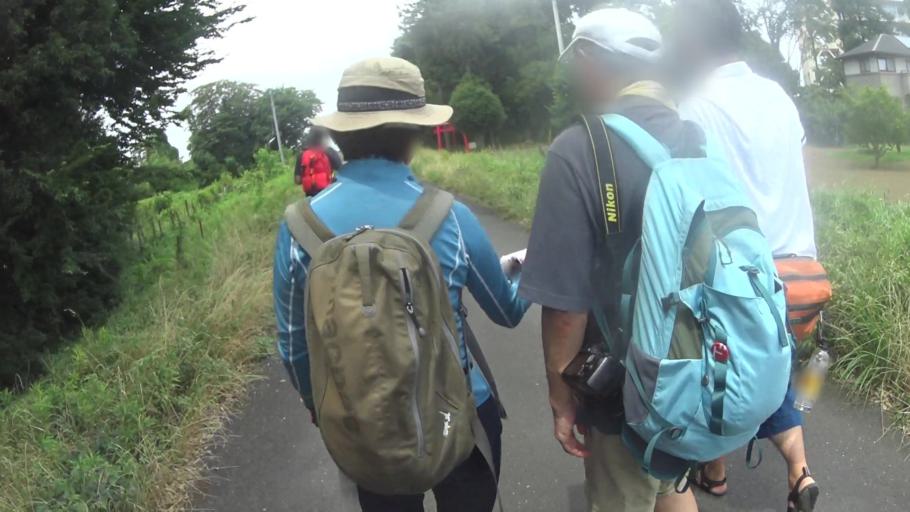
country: JP
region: Saitama
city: Okegawa
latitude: 35.9371
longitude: 139.5523
